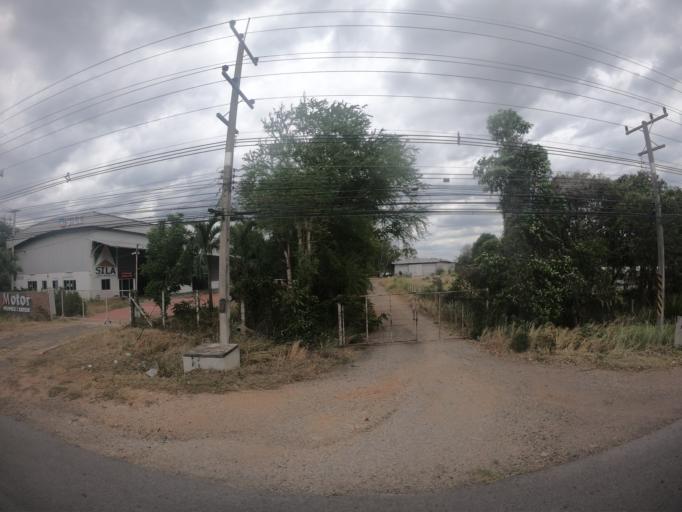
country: TH
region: Nakhon Ratchasima
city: Nakhon Ratchasima
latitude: 14.8898
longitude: 102.1673
